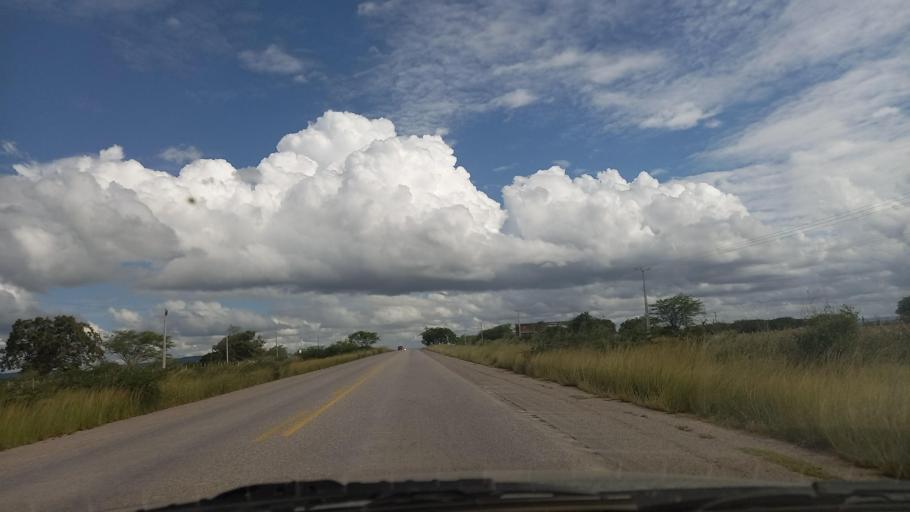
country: BR
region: Pernambuco
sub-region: Cachoeirinha
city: Cachoeirinha
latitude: -8.4644
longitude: -36.2171
